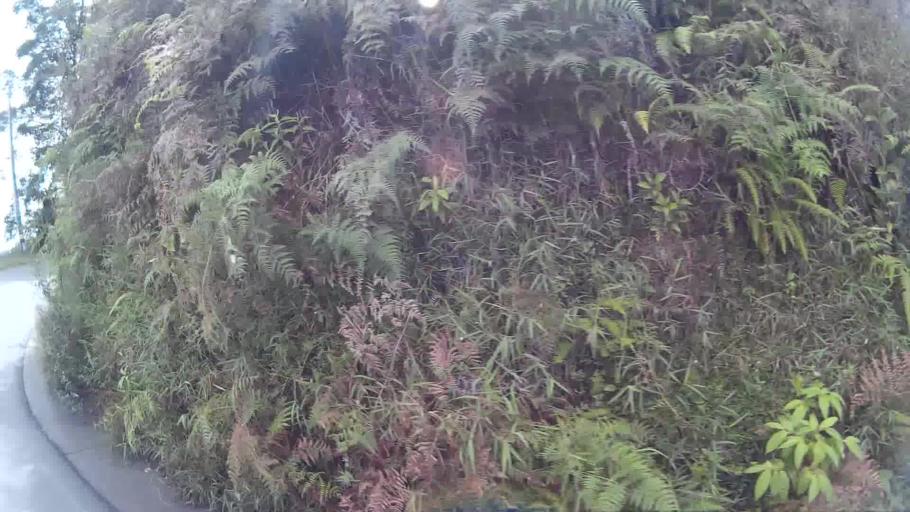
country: CO
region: Risaralda
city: Marsella
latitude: 4.8826
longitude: -75.7542
